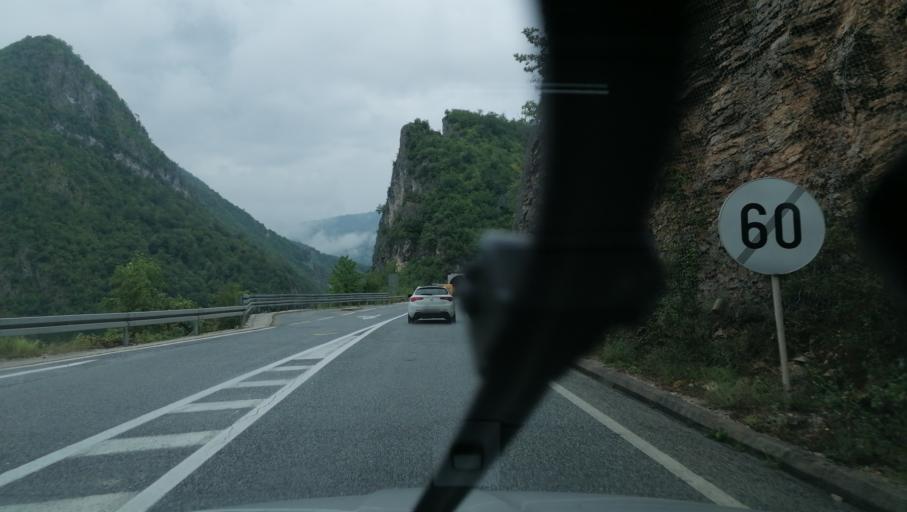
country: BA
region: Republika Srpska
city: Visegrad
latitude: 43.7386
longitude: 19.2093
